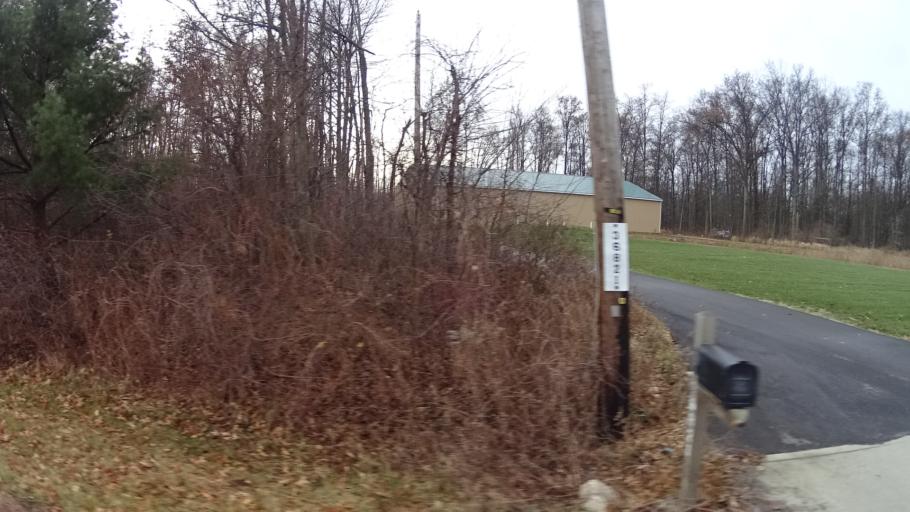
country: US
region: Ohio
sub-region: Lorain County
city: North Ridgeville
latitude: 41.3740
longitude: -82.0303
